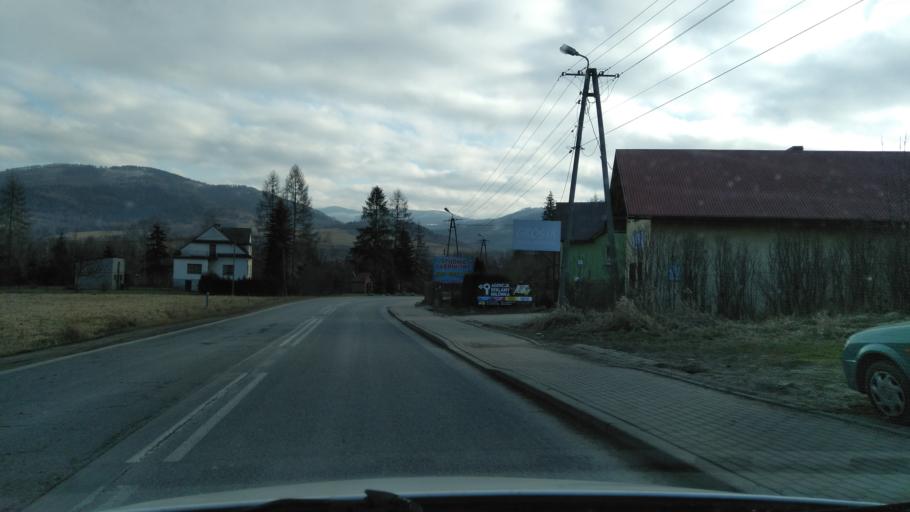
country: PL
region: Silesian Voivodeship
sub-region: Powiat zywiecki
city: Milowka
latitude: 49.5622
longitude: 19.0794
